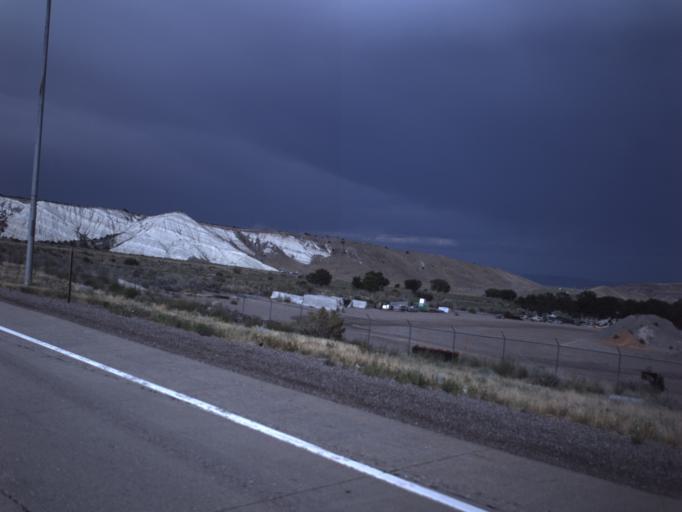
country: US
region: Utah
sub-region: Sevier County
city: Monroe
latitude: 38.5956
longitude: -112.2543
